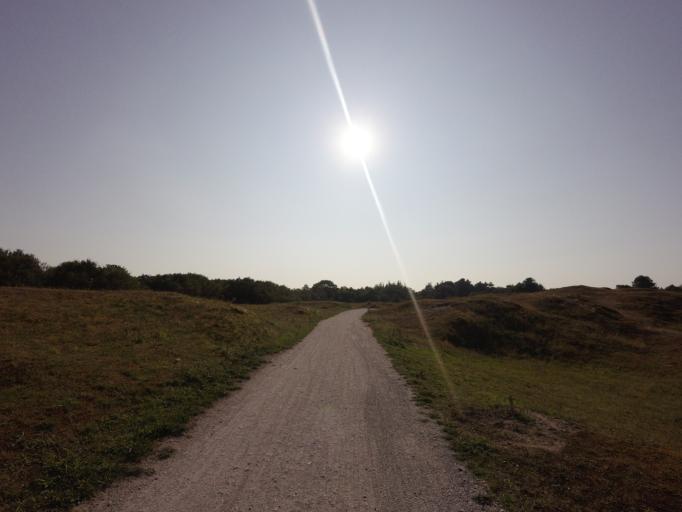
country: NL
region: Friesland
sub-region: Gemeente Schiermonnikoog
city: Schiermonnikoog
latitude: 53.4852
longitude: 6.1714
